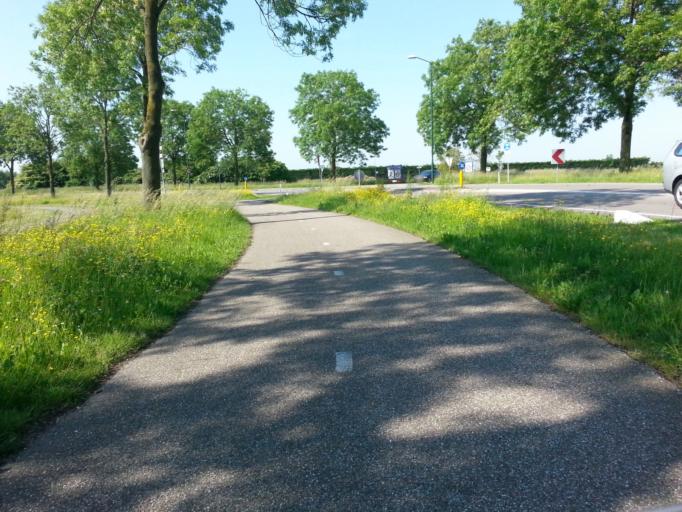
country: NL
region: Utrecht
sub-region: Gemeente Wijk bij Duurstede
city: Wijk bij Duurstede
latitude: 51.9832
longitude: 5.3258
